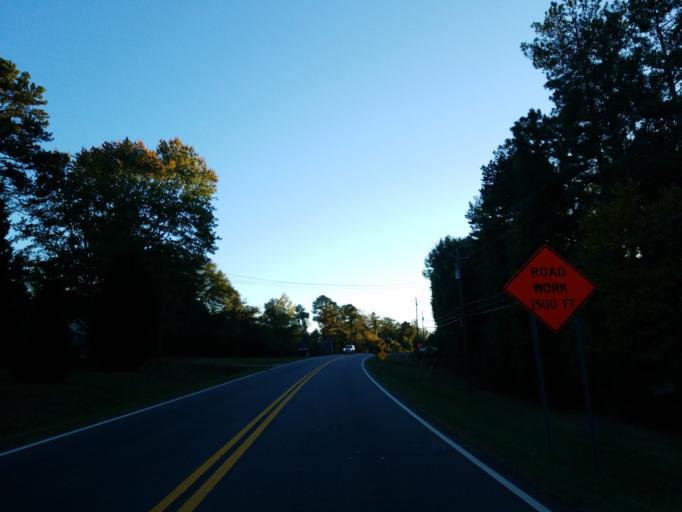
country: US
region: Georgia
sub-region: Forsyth County
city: Cumming
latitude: 34.2534
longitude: -84.1067
